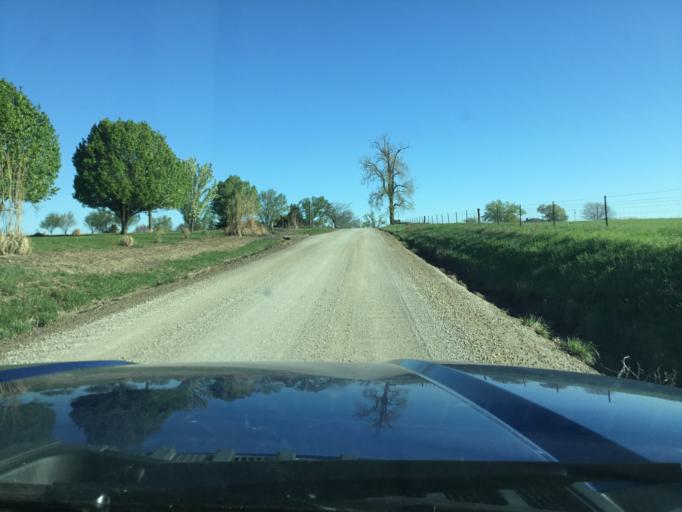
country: US
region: Kansas
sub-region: Douglas County
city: Lawrence
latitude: 38.9662
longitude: -95.3725
